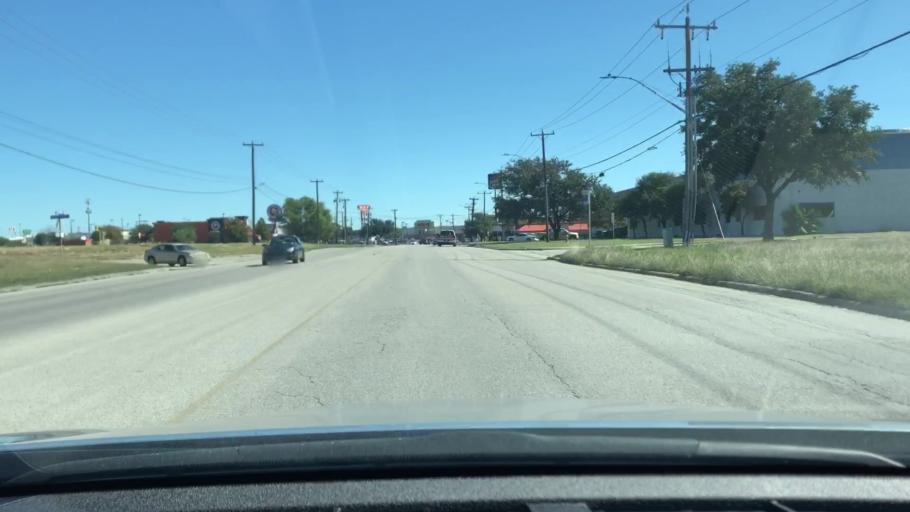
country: US
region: Texas
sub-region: Bexar County
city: Kirby
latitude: 29.4757
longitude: -98.3577
